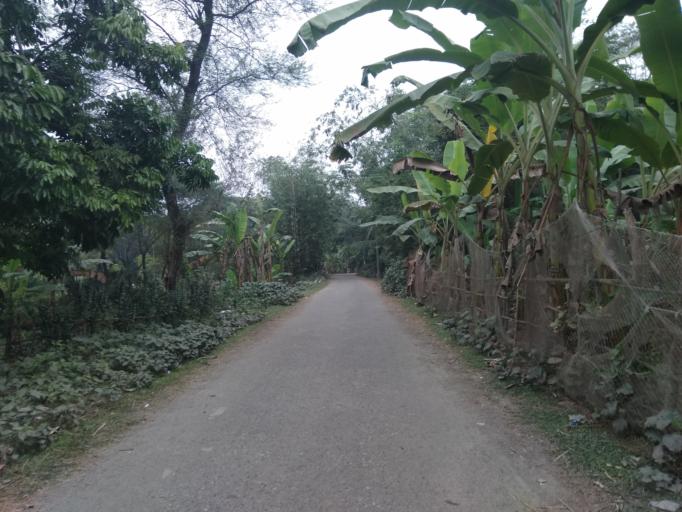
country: BD
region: Barisal
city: Mehendiganj
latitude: 22.9217
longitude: 90.3916
